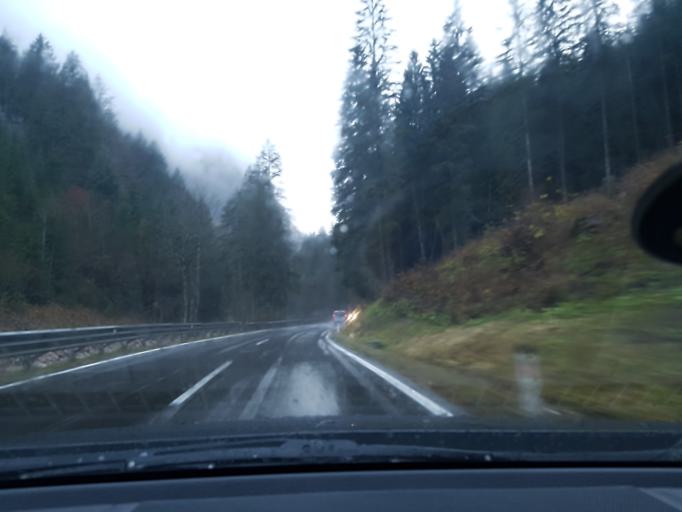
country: AT
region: Styria
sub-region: Politischer Bezirk Murtal
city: Hohentauern
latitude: 47.4501
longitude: 14.5020
